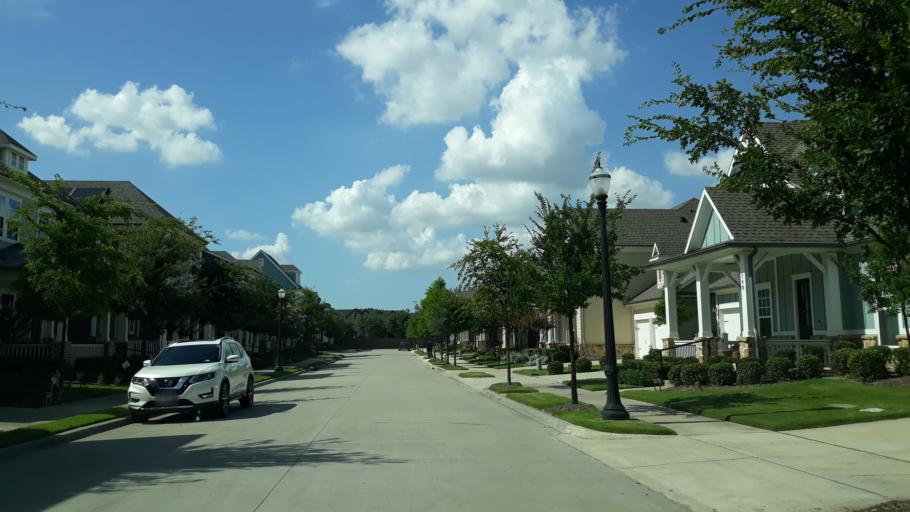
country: US
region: Texas
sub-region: Dallas County
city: Coppell
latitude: 32.9526
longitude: -97.0043
